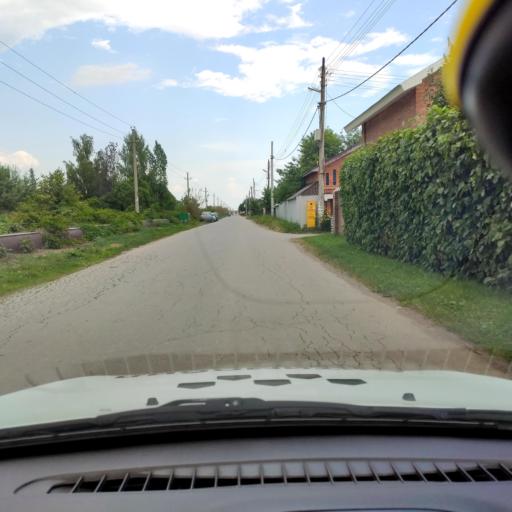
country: RU
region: Samara
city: Podstepki
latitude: 53.5074
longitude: 49.1436
